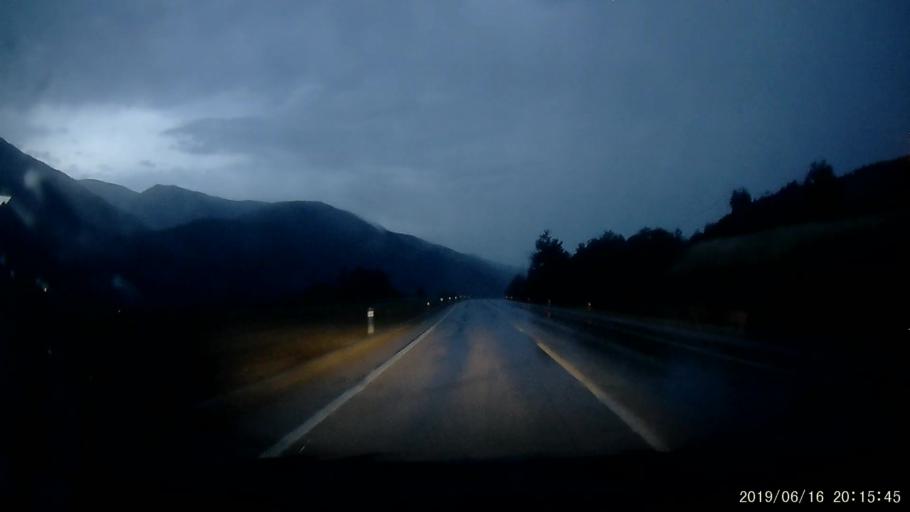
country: TR
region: Tokat
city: Resadiye
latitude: 40.3560
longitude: 37.4566
